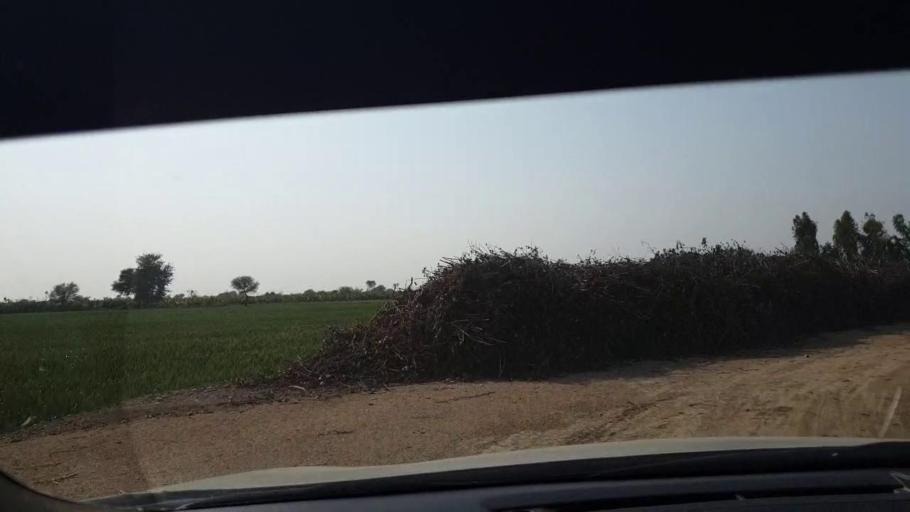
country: PK
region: Sindh
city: Tando Adam
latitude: 25.8456
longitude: 68.7219
